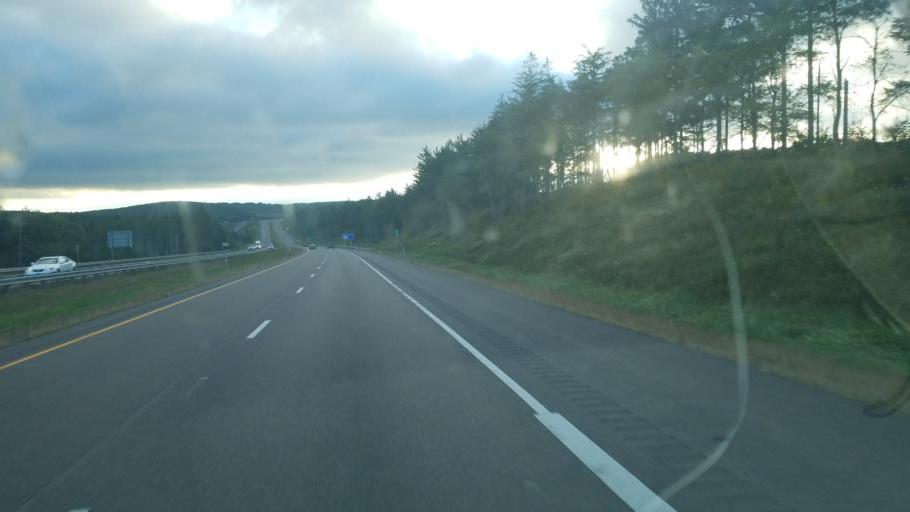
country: US
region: Maryland
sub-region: Allegany County
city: Frostburg
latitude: 39.6837
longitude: -78.9972
